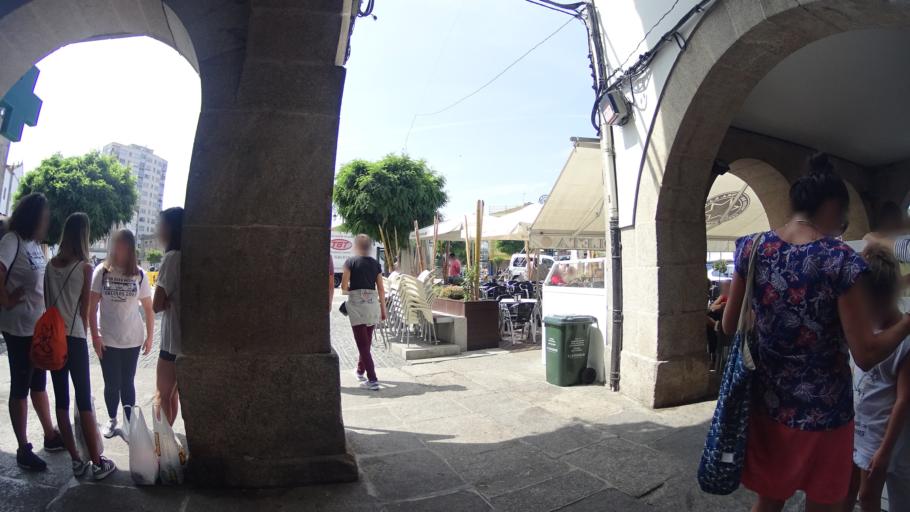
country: ES
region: Galicia
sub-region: Provincia da Coruna
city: Betanzos
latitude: 43.2798
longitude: -8.2097
